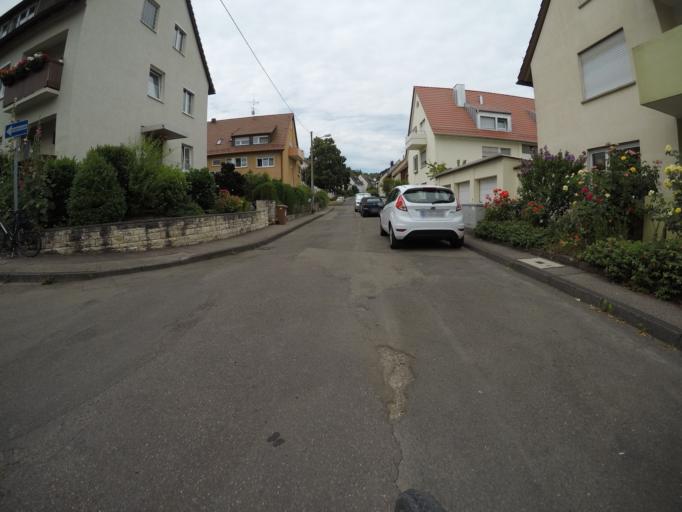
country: DE
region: Baden-Wuerttemberg
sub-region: Regierungsbezirk Stuttgart
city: Stuttgart-Ost
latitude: 48.7799
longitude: 9.2202
